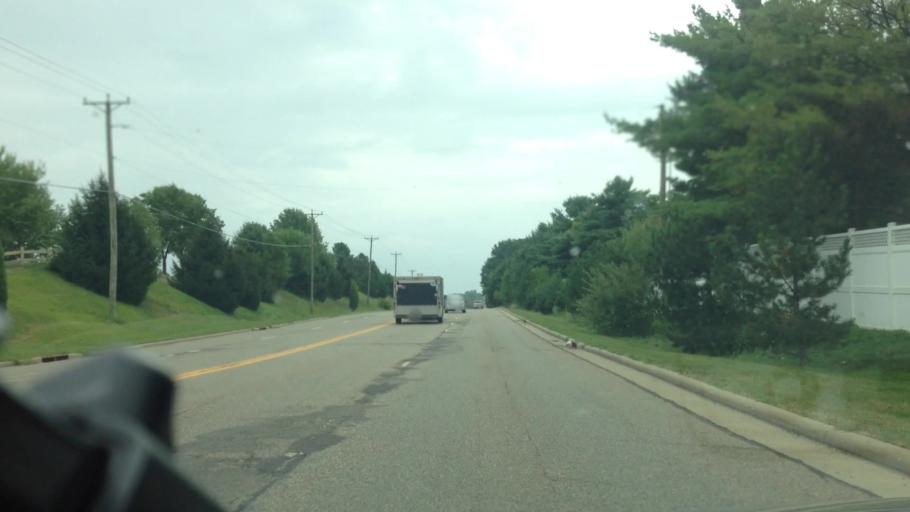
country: US
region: Ohio
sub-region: Stark County
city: Perry Heights
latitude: 40.8343
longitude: -81.4676
